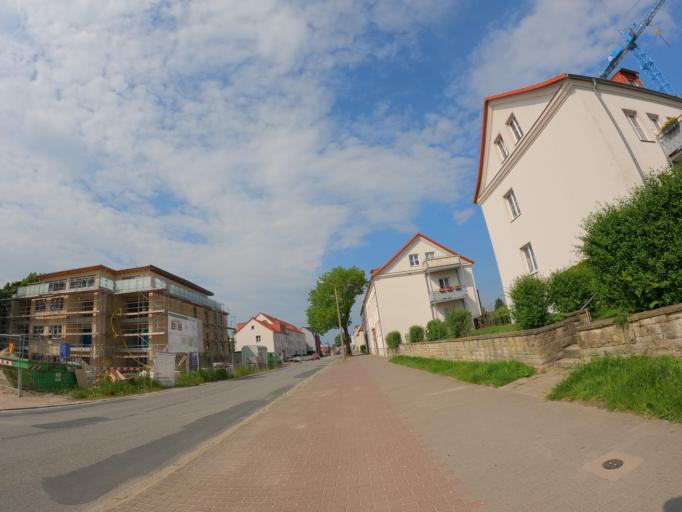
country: DE
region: Mecklenburg-Vorpommern
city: Stralsund
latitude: 54.3042
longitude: 13.0646
